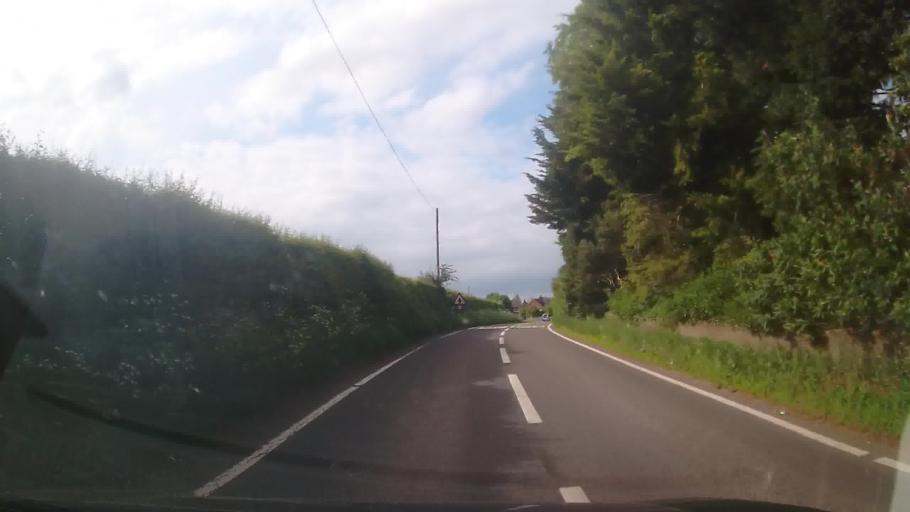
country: GB
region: England
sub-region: Shropshire
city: Petton
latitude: 52.8270
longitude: -2.8056
